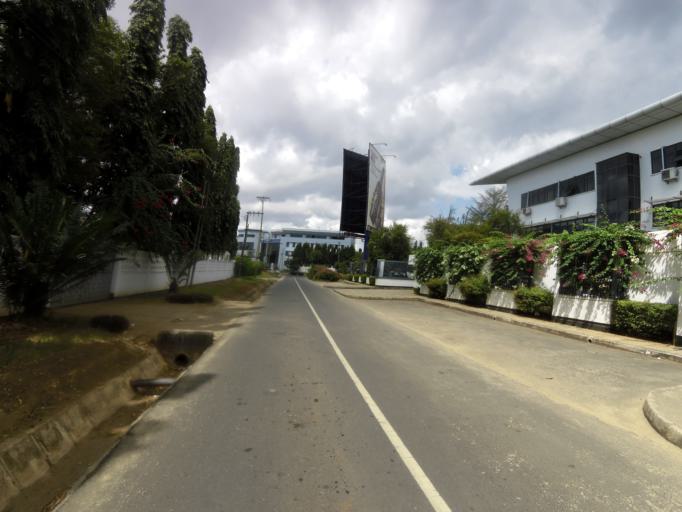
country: TZ
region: Dar es Salaam
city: Magomeni
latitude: -6.7892
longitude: 39.2797
